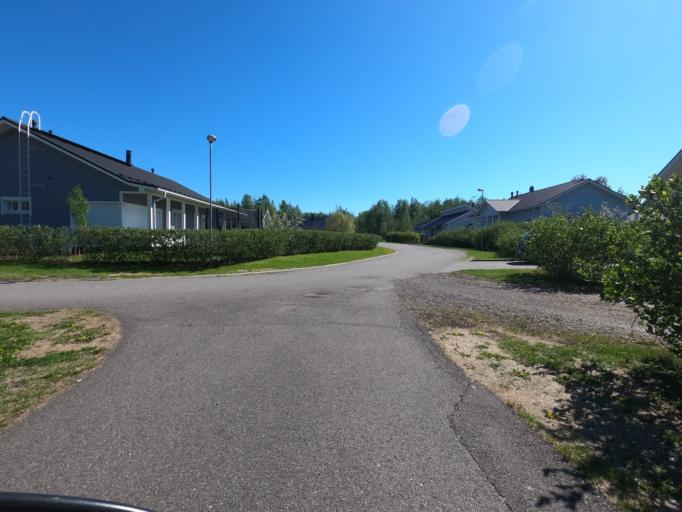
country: FI
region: North Karelia
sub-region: Joensuu
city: Joensuu
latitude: 62.6041
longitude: 29.8251
